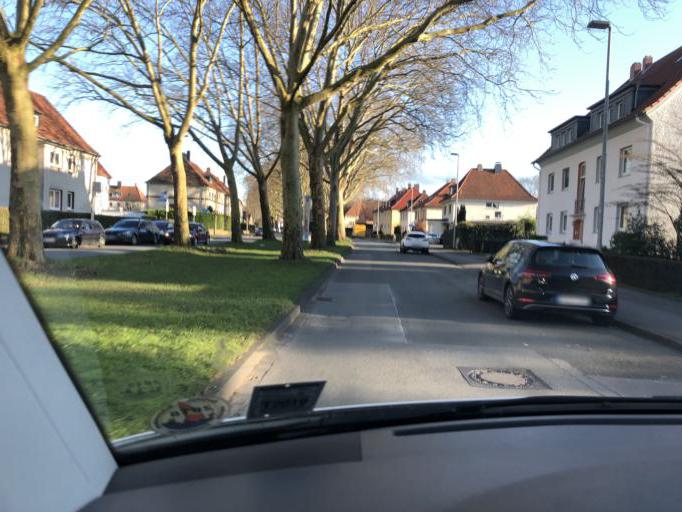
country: DE
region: North Rhine-Westphalia
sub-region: Regierungsbezirk Arnsberg
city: Soest
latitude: 51.5687
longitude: 8.0908
